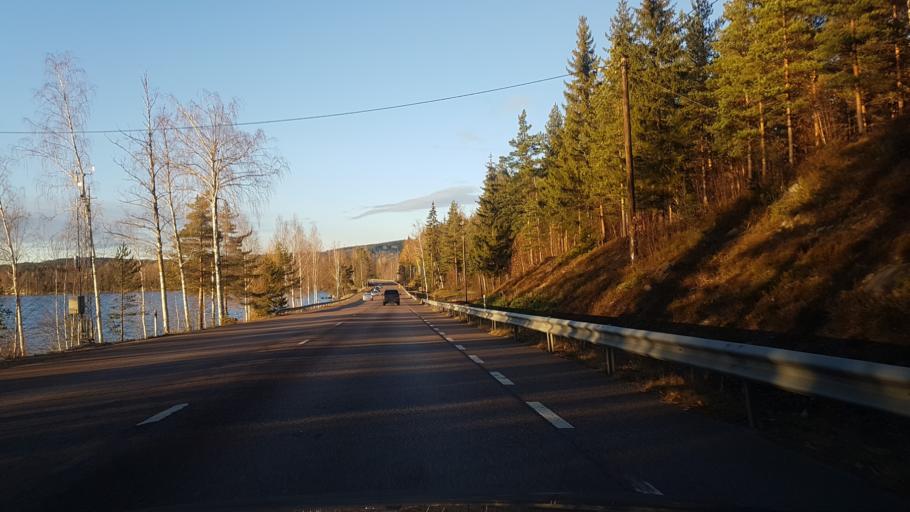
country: SE
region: Dalarna
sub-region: Faluns Kommun
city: Bjursas
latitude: 60.7134
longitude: 15.4610
